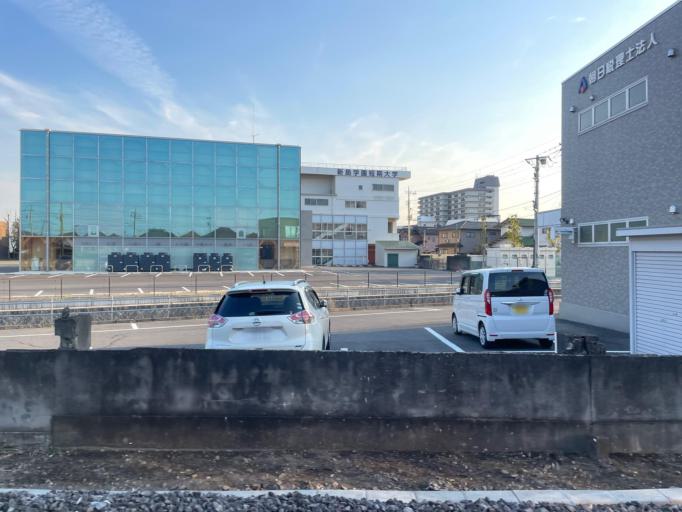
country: JP
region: Gunma
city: Takasaki
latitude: 36.3378
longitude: 139.0043
